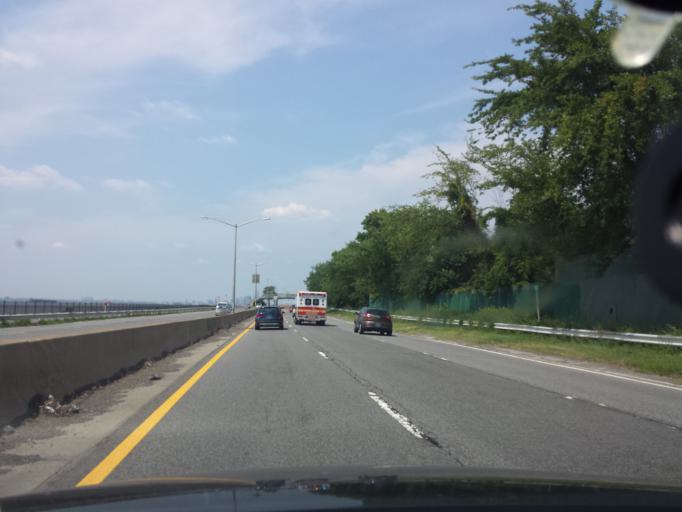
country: US
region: New York
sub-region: Kings County
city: Bensonhurst
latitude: 40.6271
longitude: -74.0412
